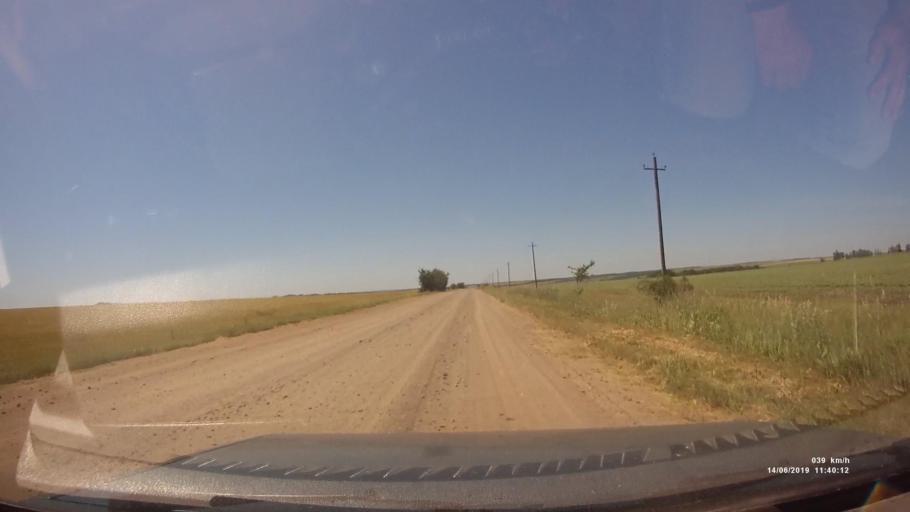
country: RU
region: Rostov
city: Kazanskaya
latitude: 49.8679
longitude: 41.3614
